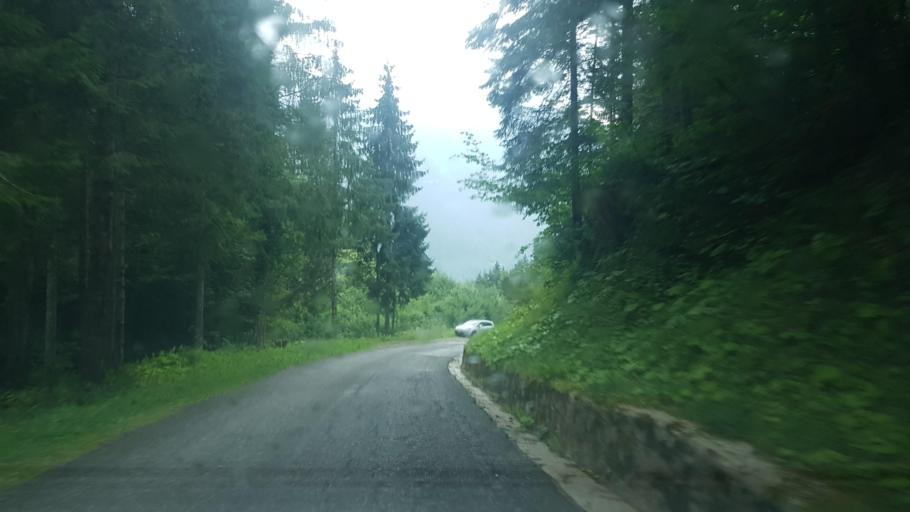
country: IT
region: Friuli Venezia Giulia
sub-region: Provincia di Udine
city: Rigolato
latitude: 46.5515
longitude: 12.8346
